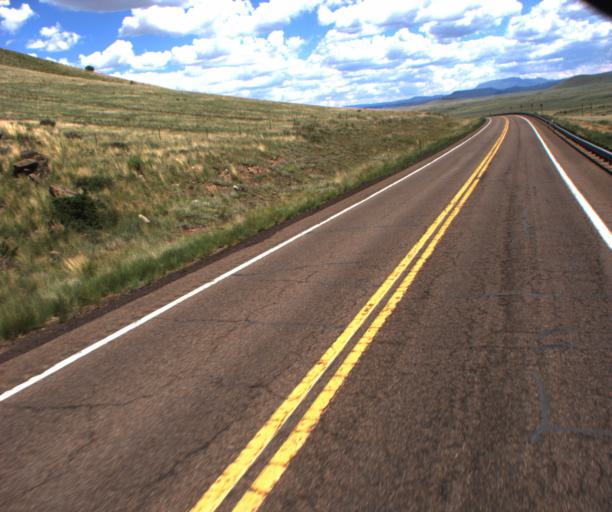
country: US
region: Arizona
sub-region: Apache County
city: Springerville
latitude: 34.2097
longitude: -109.4258
